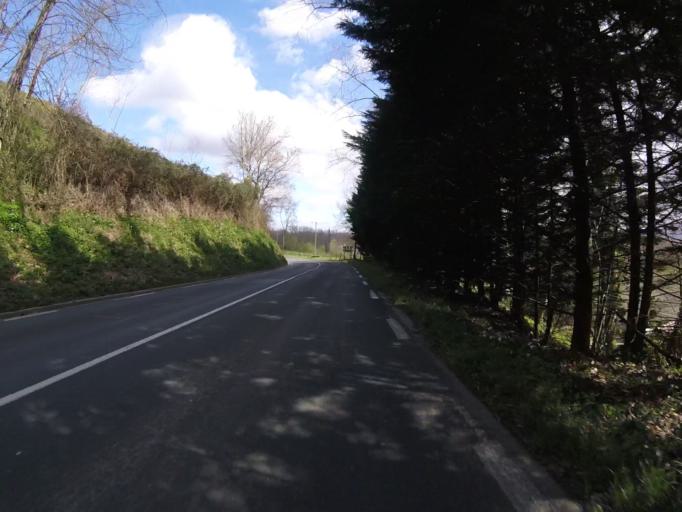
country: ES
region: Basque Country
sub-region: Provincia de Guipuzcoa
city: Errenteria
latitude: 43.2862
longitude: -1.9109
